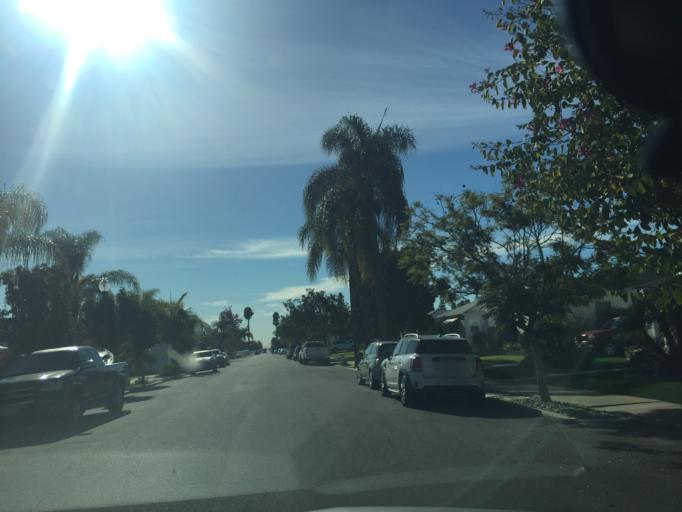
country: US
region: California
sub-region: San Diego County
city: Lemon Grove
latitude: 32.7625
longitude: -117.0868
